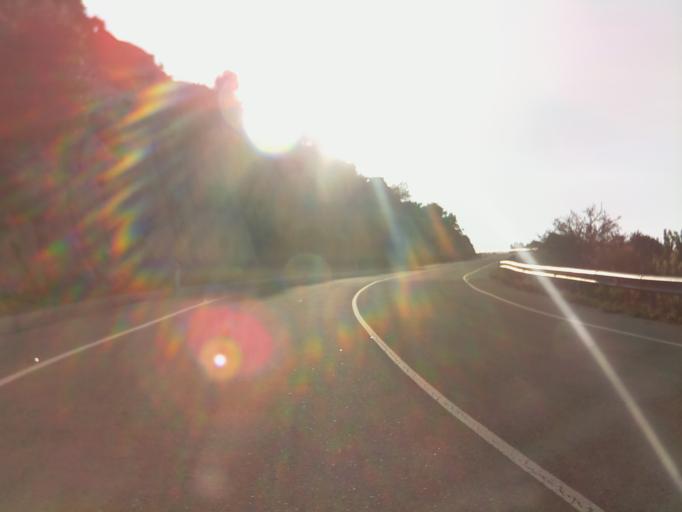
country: CY
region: Pafos
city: Pegeia
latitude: 34.8922
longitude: 32.3571
